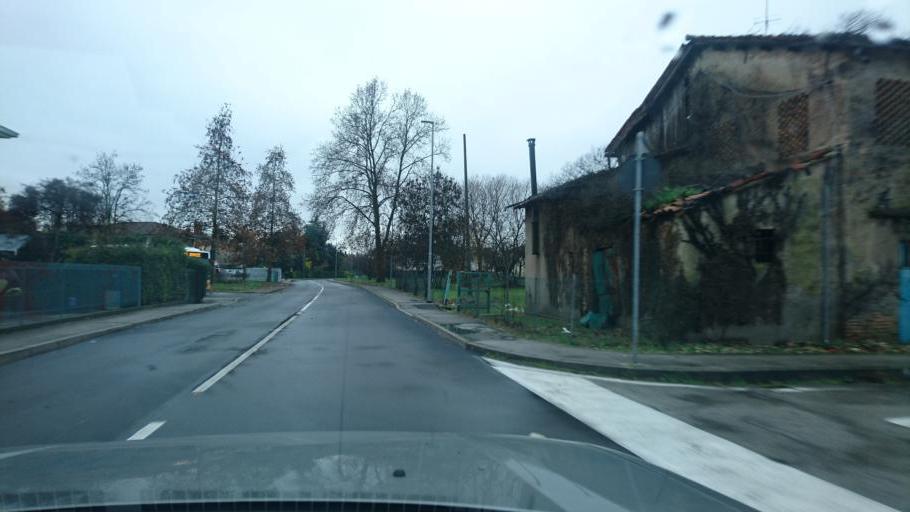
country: IT
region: Veneto
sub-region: Provincia di Padova
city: Ponte San Nicolo
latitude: 45.3795
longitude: 11.9399
